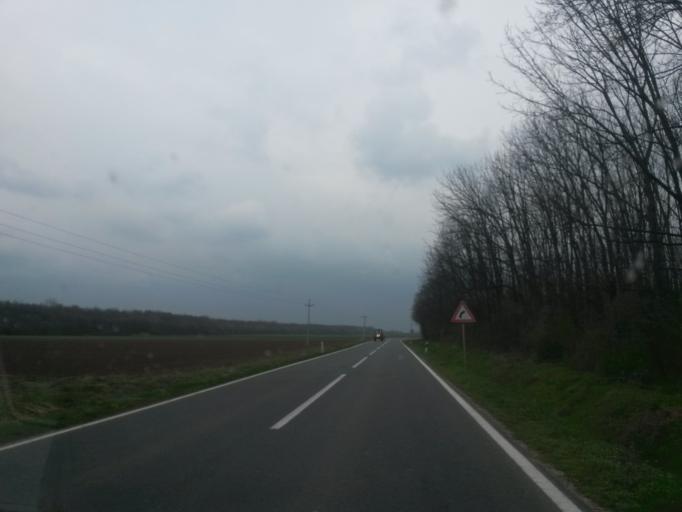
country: HR
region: Vukovarsko-Srijemska
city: Nijemci
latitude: 45.1984
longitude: 19.0191
